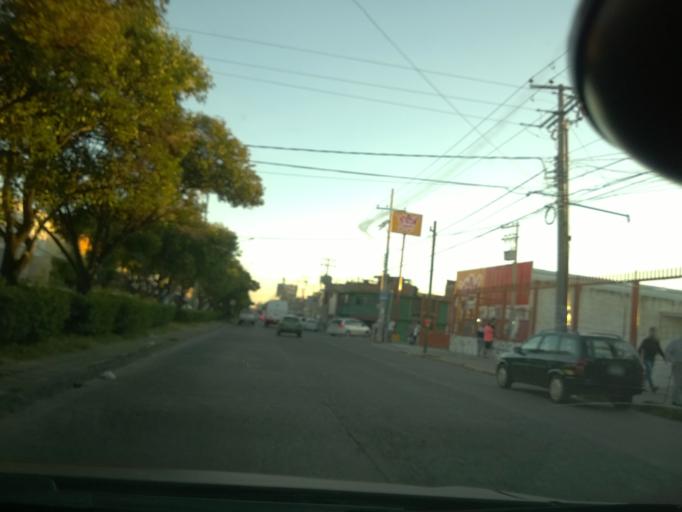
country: MX
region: Guanajuato
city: Leon
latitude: 21.1085
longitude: -101.6774
